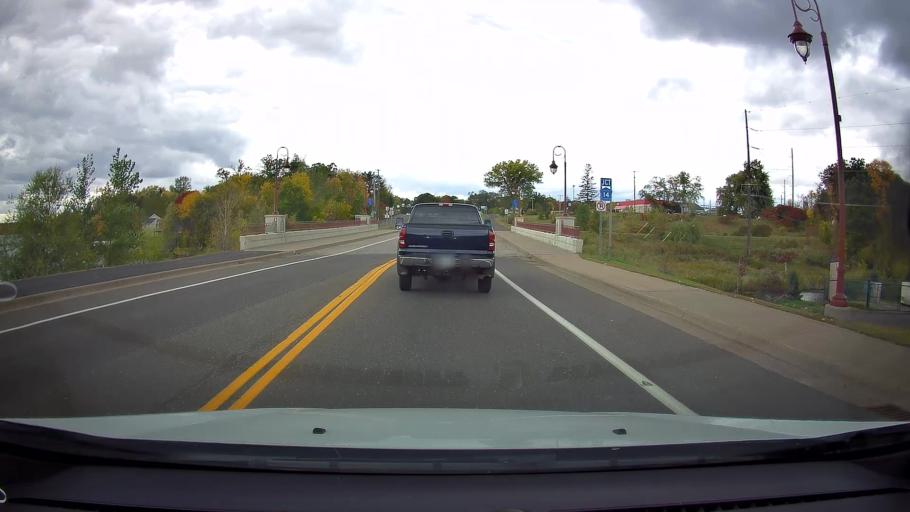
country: US
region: Minnesota
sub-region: Chisago County
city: Lindstrom
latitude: 45.3906
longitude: -92.8526
